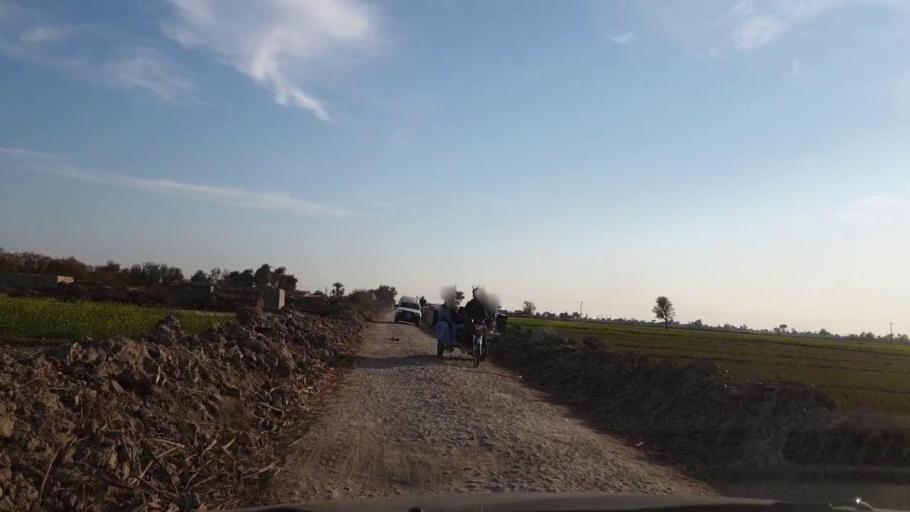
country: PK
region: Sindh
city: Khadro
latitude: 26.1735
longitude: 68.7529
